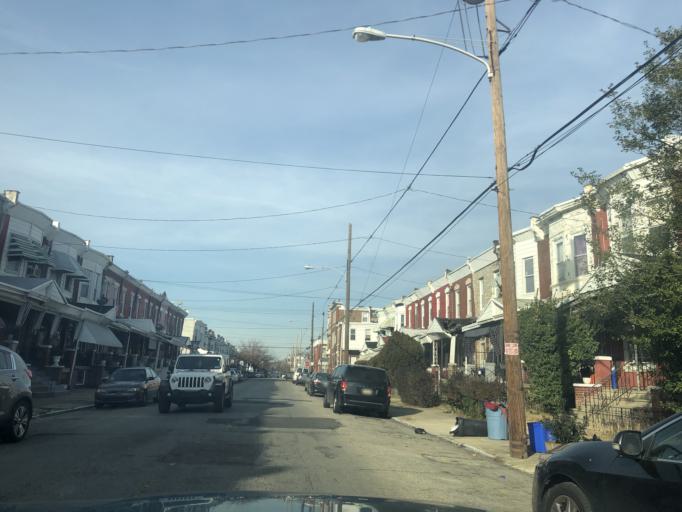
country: US
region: Pennsylvania
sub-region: Delaware County
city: Millbourne
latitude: 39.9713
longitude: -75.2327
